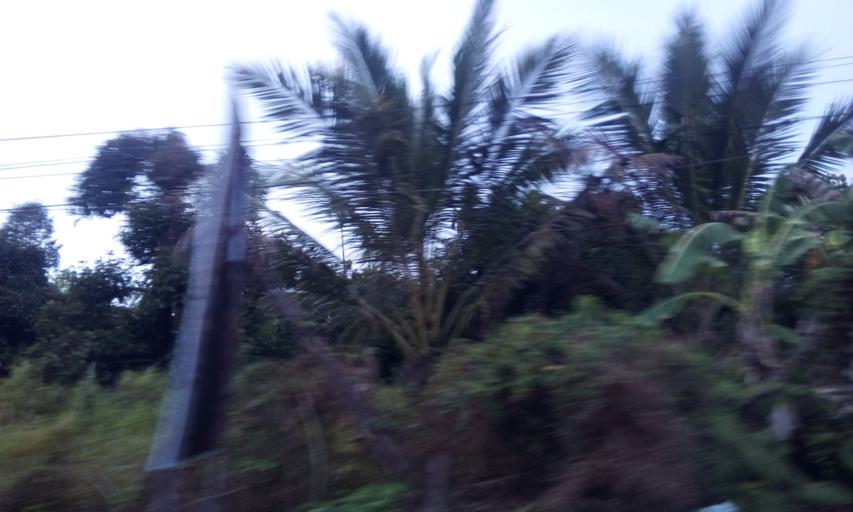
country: TH
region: Trat
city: Khao Saming
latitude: 12.3623
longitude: 102.3843
